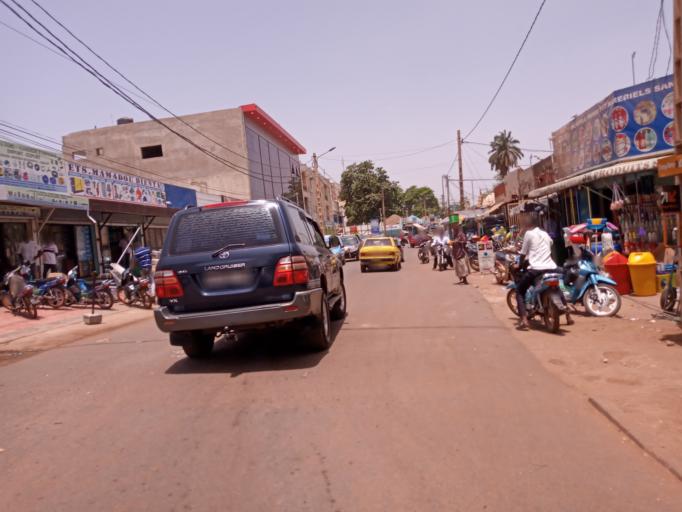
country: ML
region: Bamako
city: Bamako
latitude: 12.6368
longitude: -8.0017
